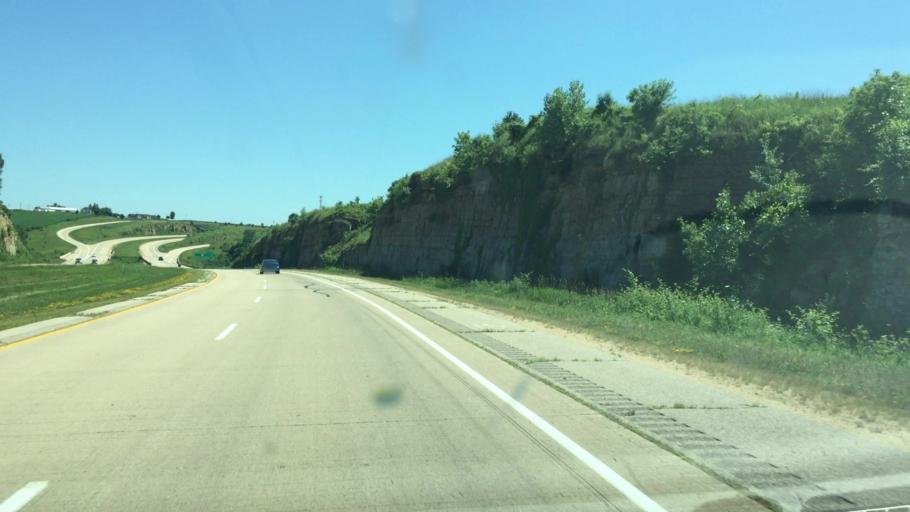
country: US
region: Wisconsin
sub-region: Iowa County
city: Mineral Point
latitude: 42.8570
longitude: -90.2031
